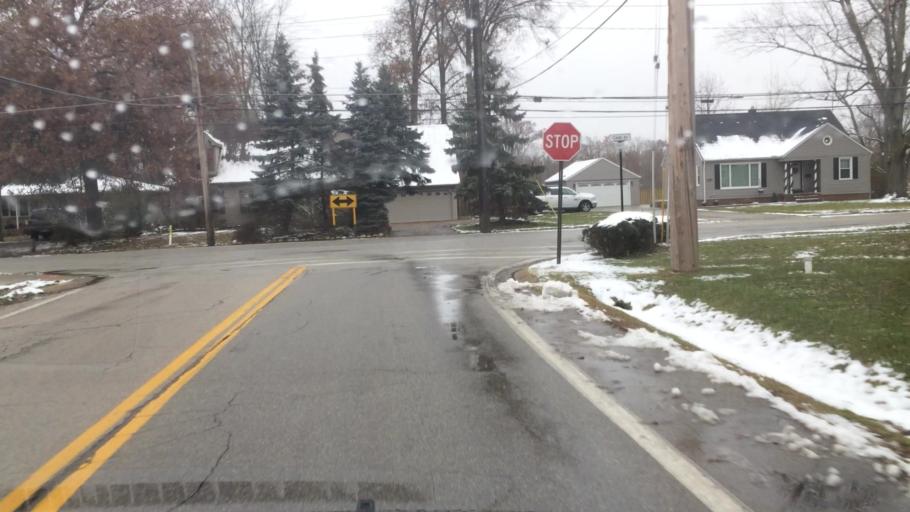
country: US
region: Ohio
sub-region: Cuyahoga County
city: Olmsted Falls
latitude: 41.3817
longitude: -81.9094
